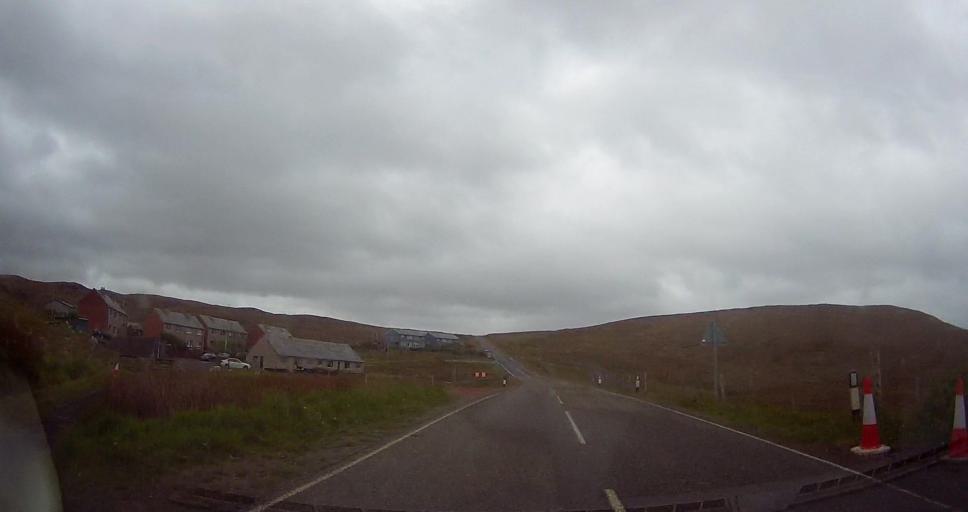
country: GB
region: Scotland
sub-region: Shetland Islands
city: Lerwick
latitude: 60.4892
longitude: -1.4515
